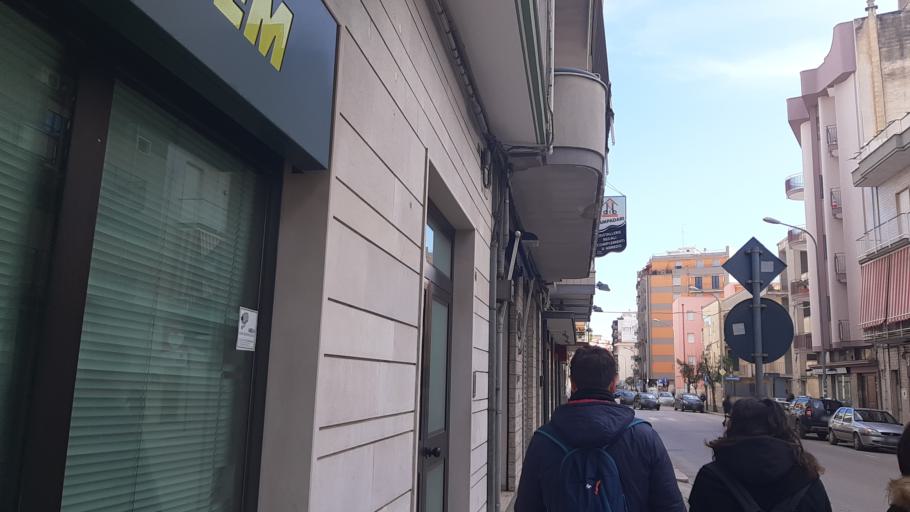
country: IT
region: Apulia
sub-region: Provincia di Barletta - Andria - Trani
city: Andria
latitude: 41.2326
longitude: 16.2967
